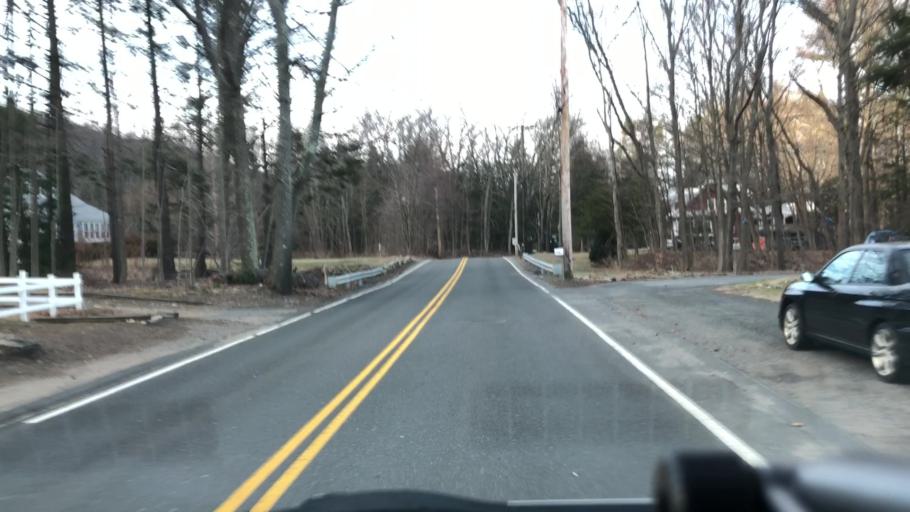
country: US
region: Massachusetts
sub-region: Hampshire County
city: Easthampton
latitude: 42.2490
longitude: -72.6536
